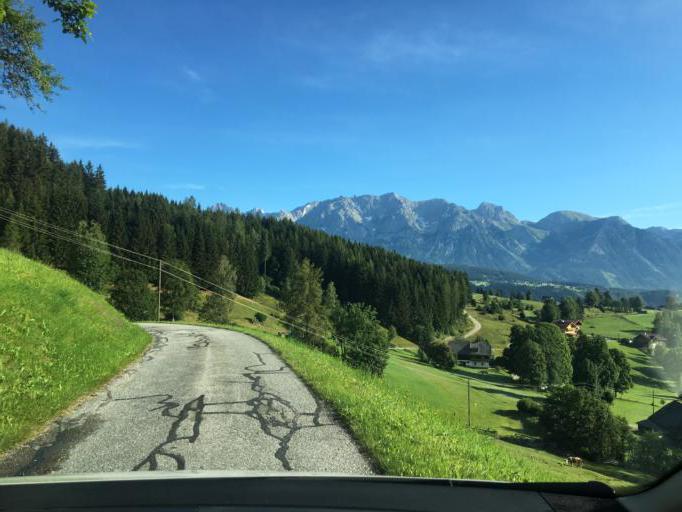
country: AT
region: Styria
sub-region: Politischer Bezirk Liezen
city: Schladming
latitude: 47.3693
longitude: 13.6625
